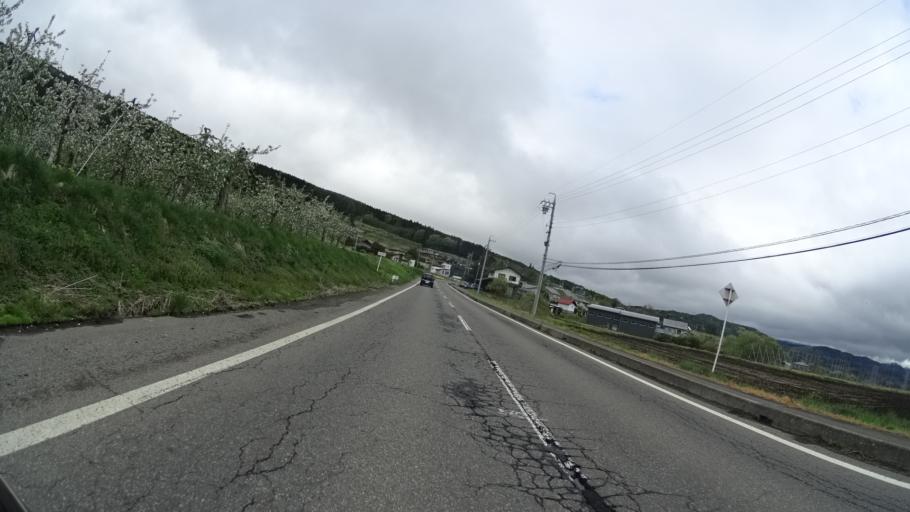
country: JP
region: Nagano
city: Nagano-shi
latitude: 36.7369
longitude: 138.2057
